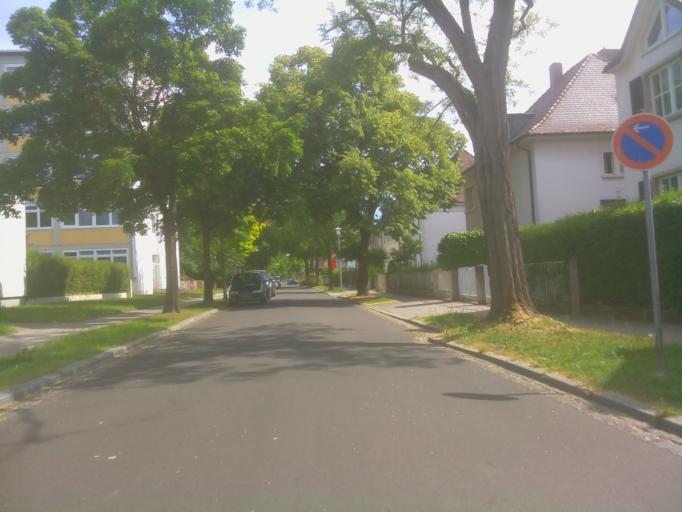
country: DE
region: Rheinland-Pfalz
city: Frankenthal
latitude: 49.5320
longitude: 8.3444
